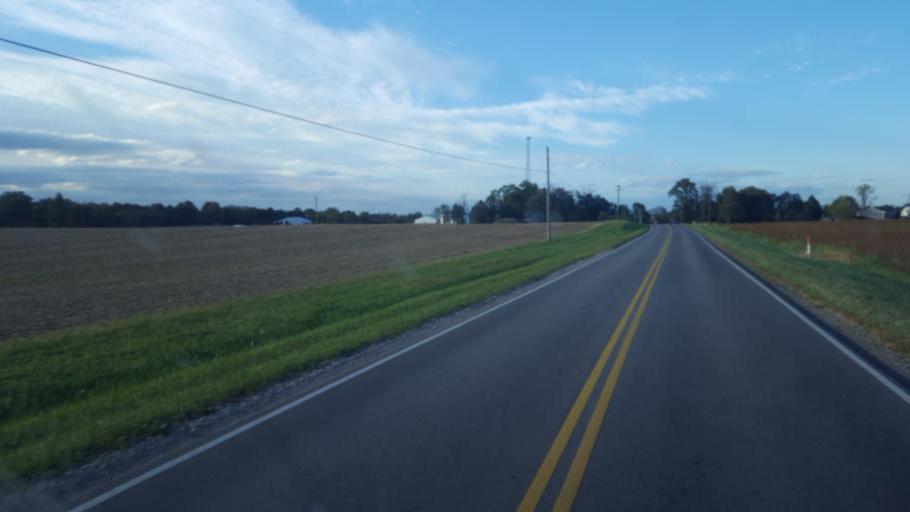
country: US
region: Ohio
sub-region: Licking County
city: Pataskala
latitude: 40.0465
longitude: -82.7333
